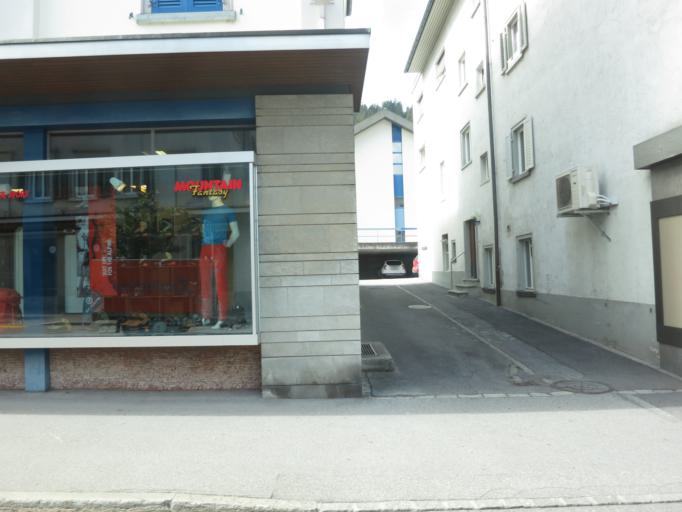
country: CH
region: Grisons
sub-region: Hinterrhein District
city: Thusis
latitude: 46.6962
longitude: 9.4395
